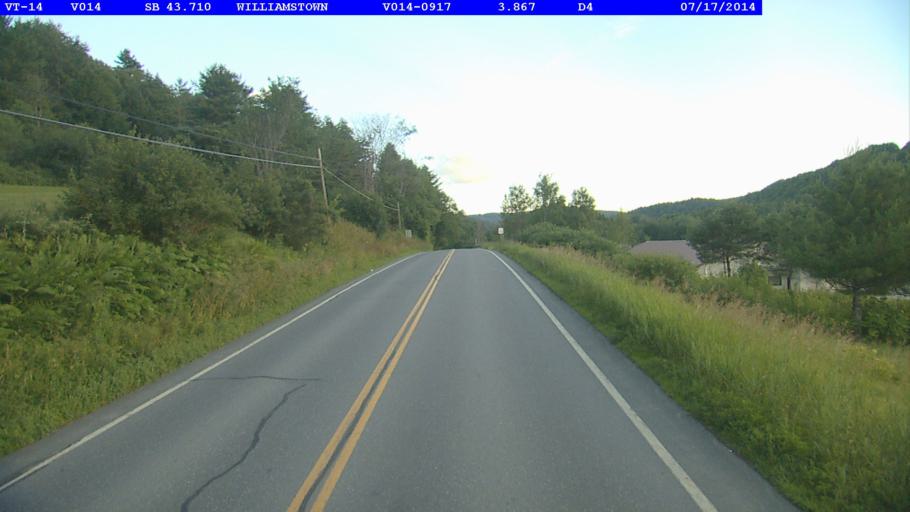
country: US
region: Vermont
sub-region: Orange County
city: Williamstown
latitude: 44.1135
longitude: -72.5397
